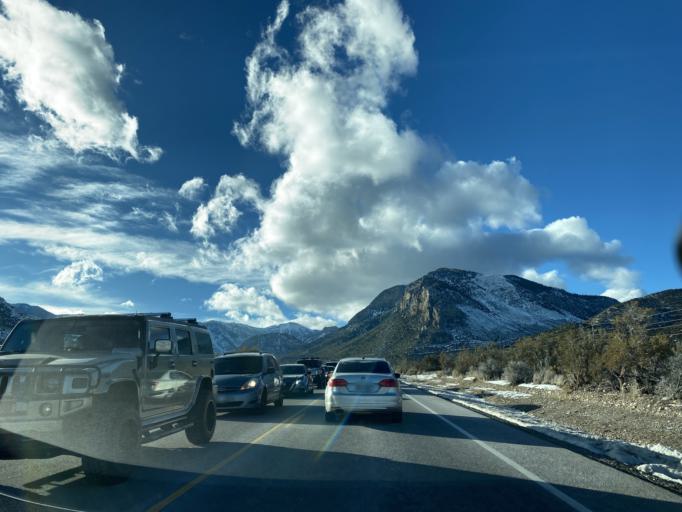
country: US
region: Nevada
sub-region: Clark County
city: Summerlin South
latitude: 36.2701
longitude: -115.5671
